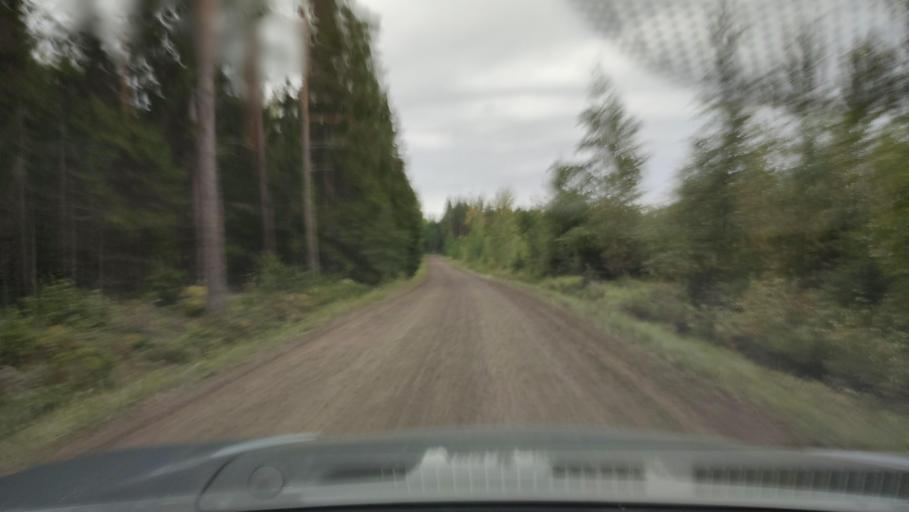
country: FI
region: Southern Ostrobothnia
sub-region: Suupohja
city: Karijoki
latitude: 62.2284
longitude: 21.5726
